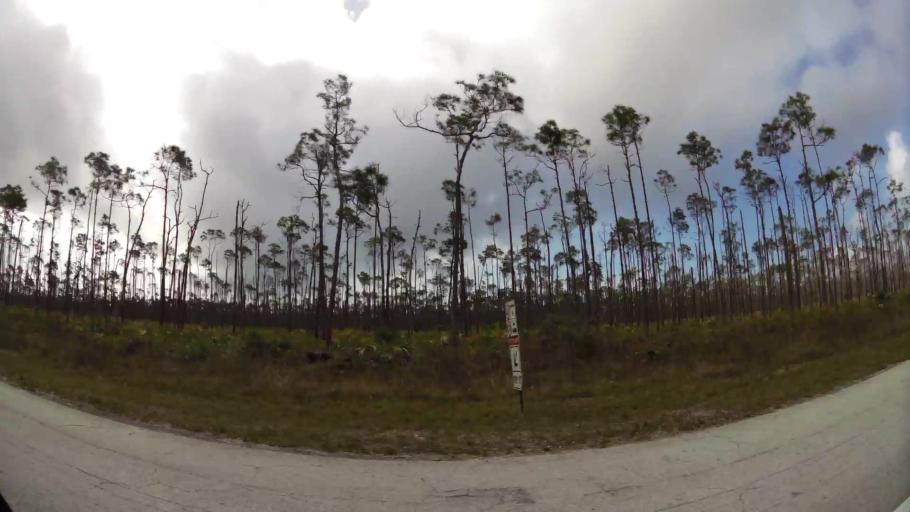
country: BS
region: Freeport
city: Lucaya
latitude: 26.5933
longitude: -78.5504
